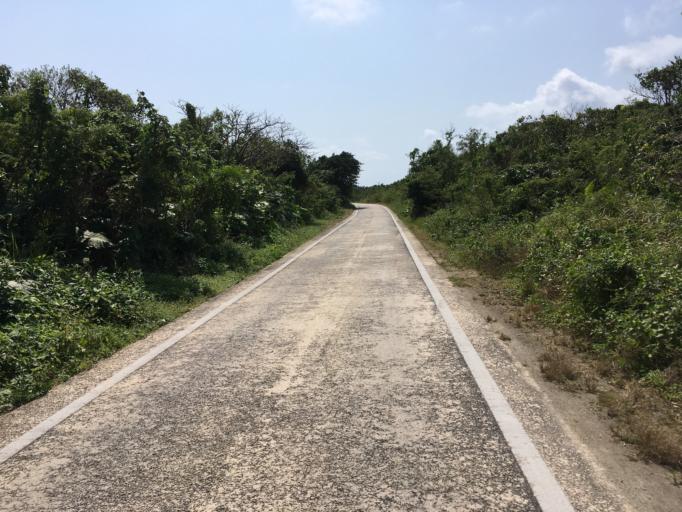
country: JP
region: Okinawa
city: Ishigaki
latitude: 24.3247
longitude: 124.0828
